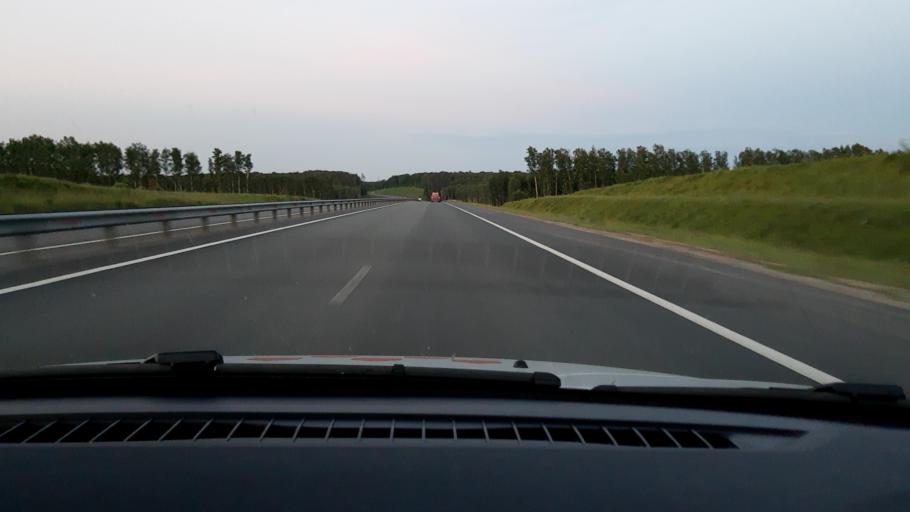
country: RU
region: Nizjnij Novgorod
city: Afonino
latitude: 56.1037
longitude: 44.0080
